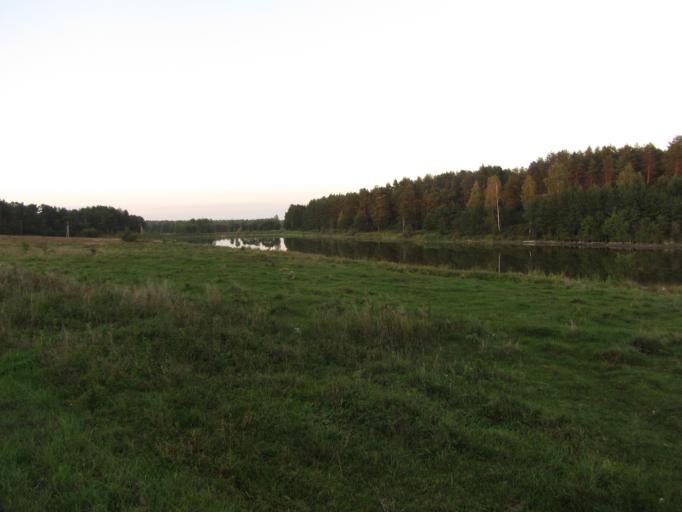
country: LT
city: Eisiskes
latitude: 54.3112
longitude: 24.9660
